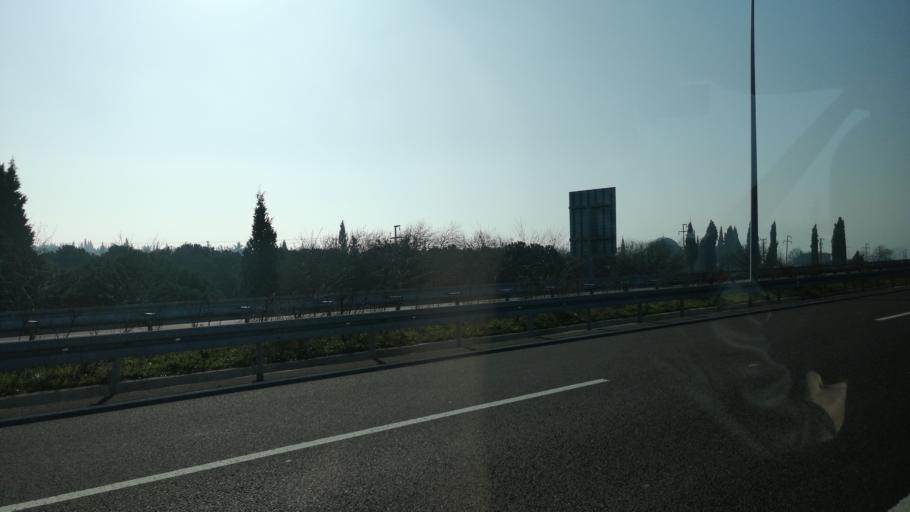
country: TR
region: Yalova
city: Altinova
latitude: 40.7261
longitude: 29.5040
